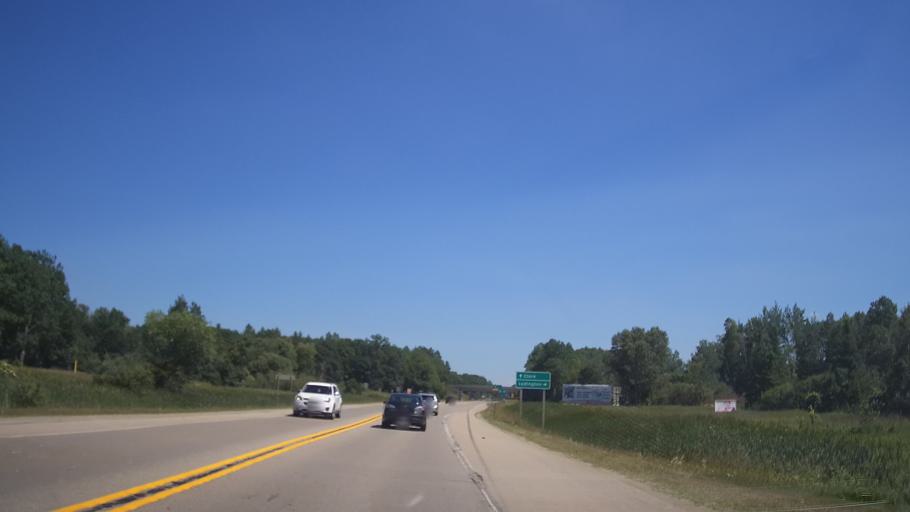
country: US
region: Michigan
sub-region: Clare County
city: Clare
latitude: 43.8676
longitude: -84.9150
